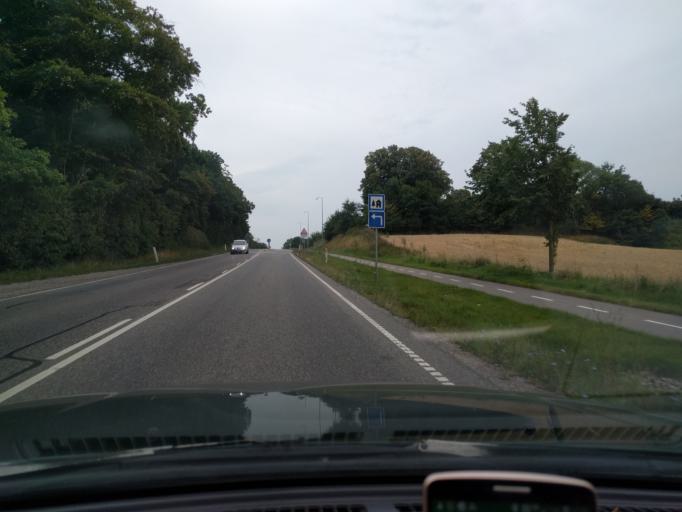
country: DK
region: Zealand
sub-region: Slagelse Kommune
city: Skaelskor
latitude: 55.2644
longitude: 11.2798
